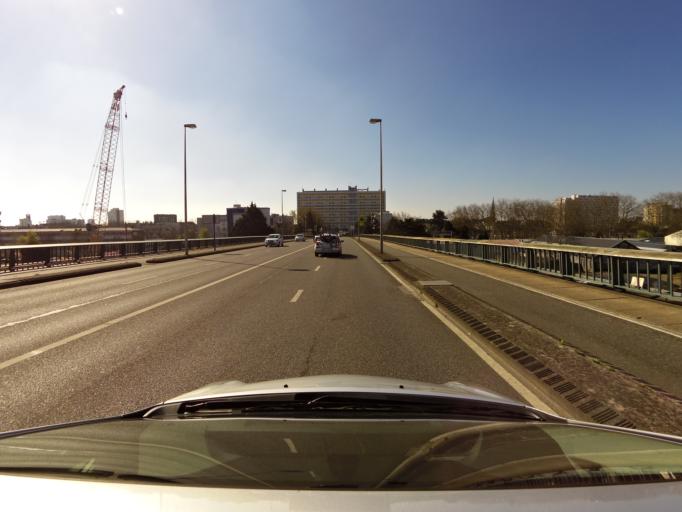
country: FR
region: Brittany
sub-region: Departement du Morbihan
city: Lorient
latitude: 47.7547
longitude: -3.3713
